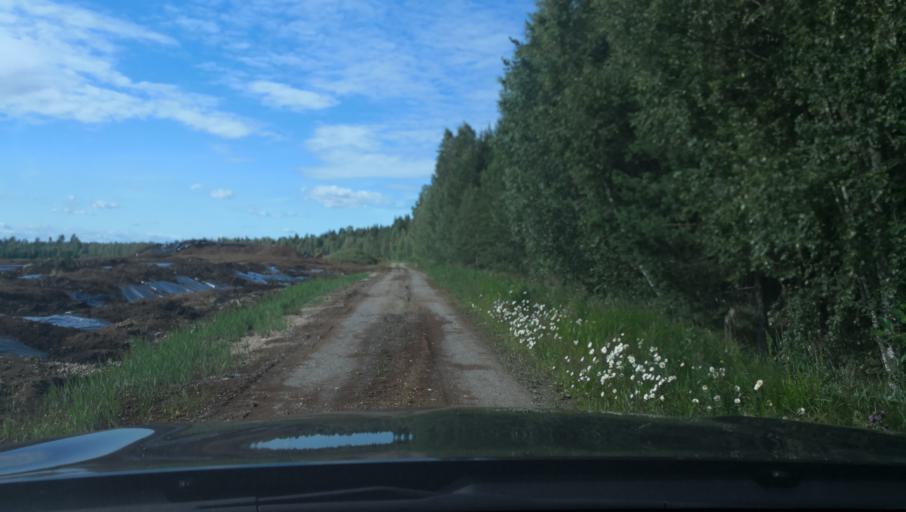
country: SE
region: Vaestmanland
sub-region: Surahammars Kommun
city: Surahammar
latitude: 59.6661
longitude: 16.1052
